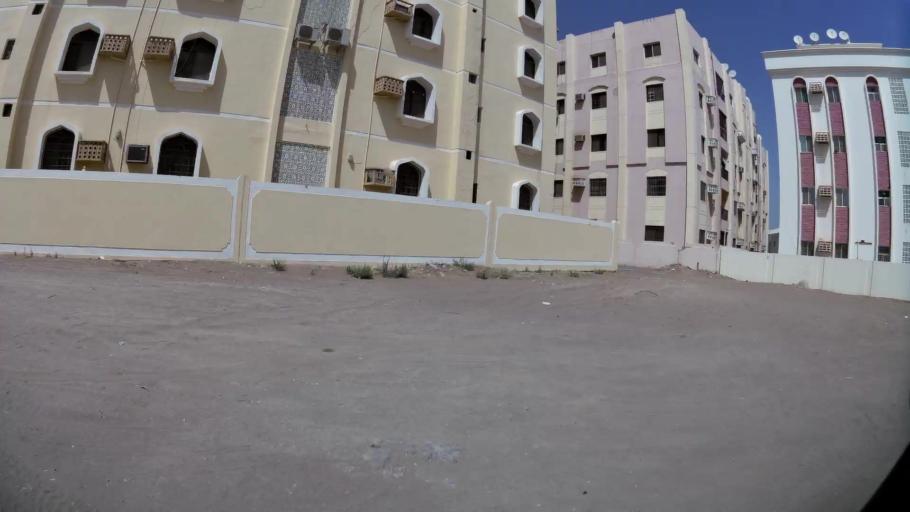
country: OM
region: Muhafazat Masqat
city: Bawshar
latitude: 23.5880
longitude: 58.4260
